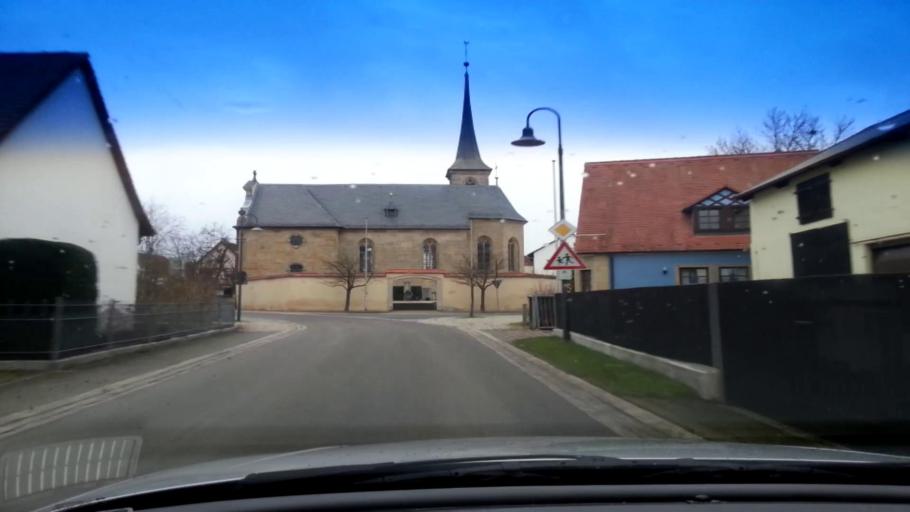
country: DE
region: Bavaria
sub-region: Upper Franconia
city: Frensdorf
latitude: 49.8236
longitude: 10.8891
